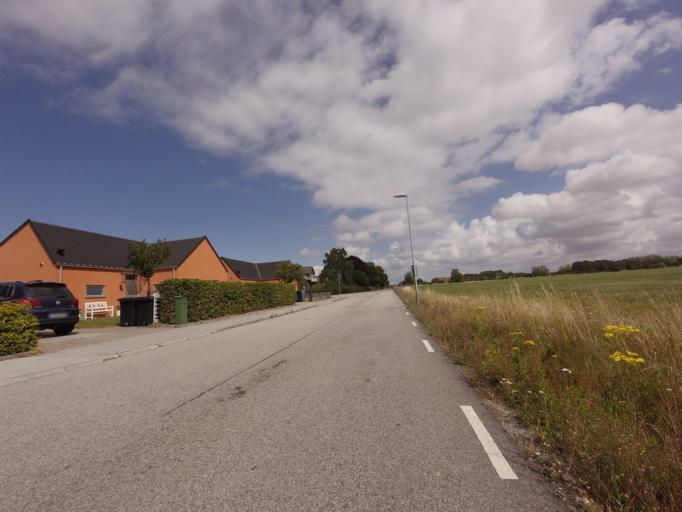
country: SE
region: Skane
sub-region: Malmo
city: Bunkeflostrand
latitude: 55.5515
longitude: 12.9621
